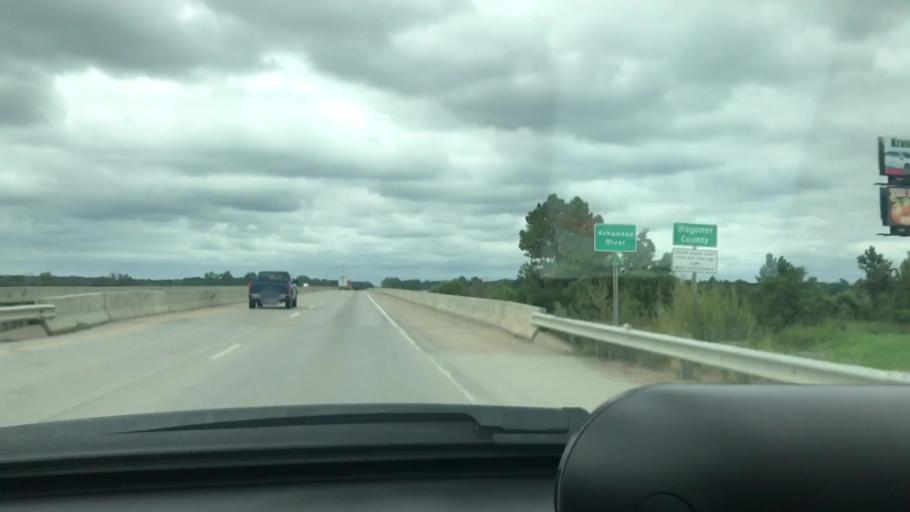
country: US
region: Oklahoma
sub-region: Muskogee County
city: Muskogee
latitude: 35.8038
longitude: -95.4017
